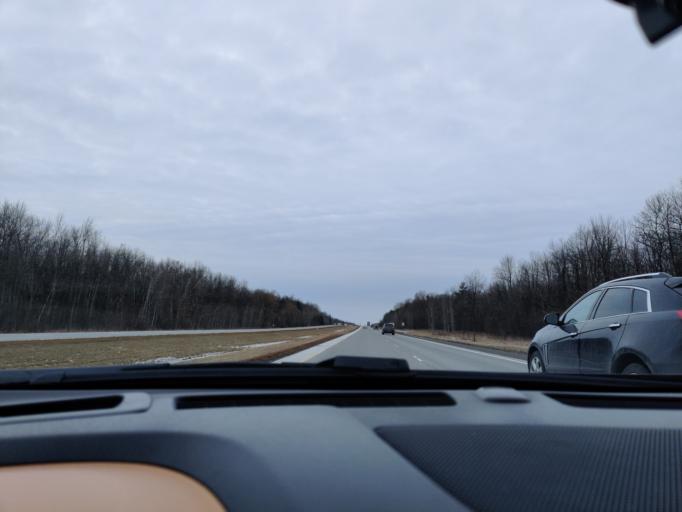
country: US
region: New York
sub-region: St. Lawrence County
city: Ogdensburg
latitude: 44.8543
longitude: -75.3358
